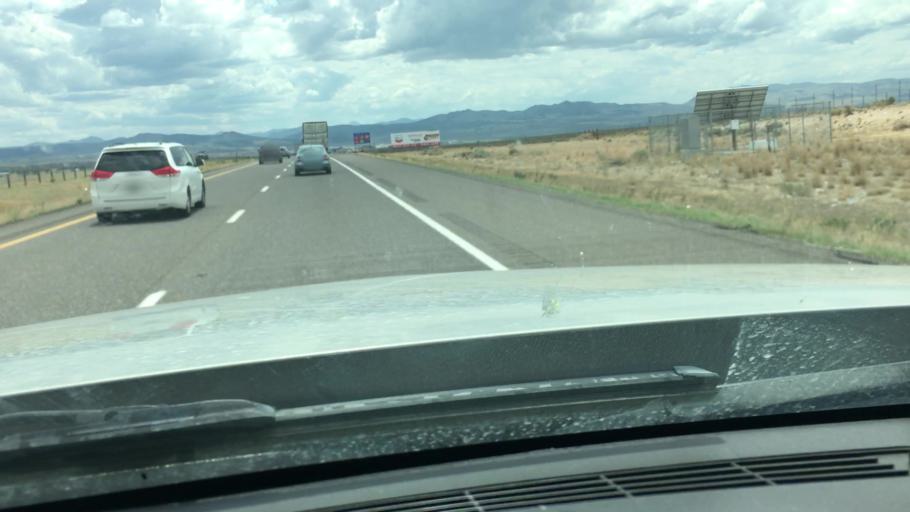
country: US
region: Utah
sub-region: Beaver County
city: Beaver
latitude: 38.3208
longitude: -112.6553
